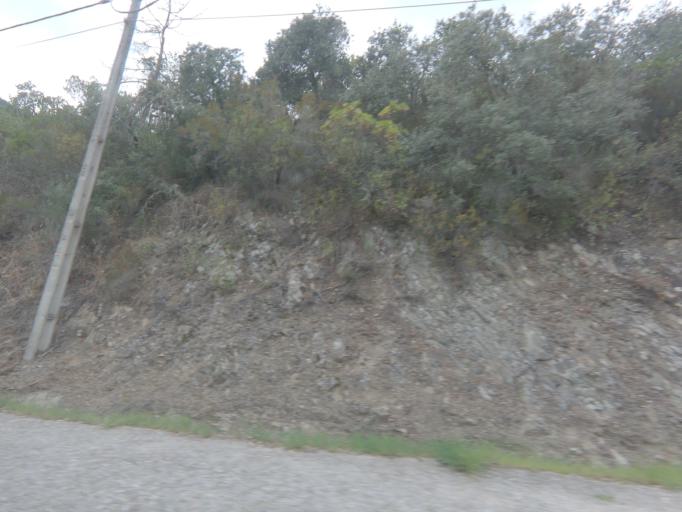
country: PT
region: Viseu
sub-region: Armamar
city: Armamar
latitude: 41.1266
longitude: -7.6428
